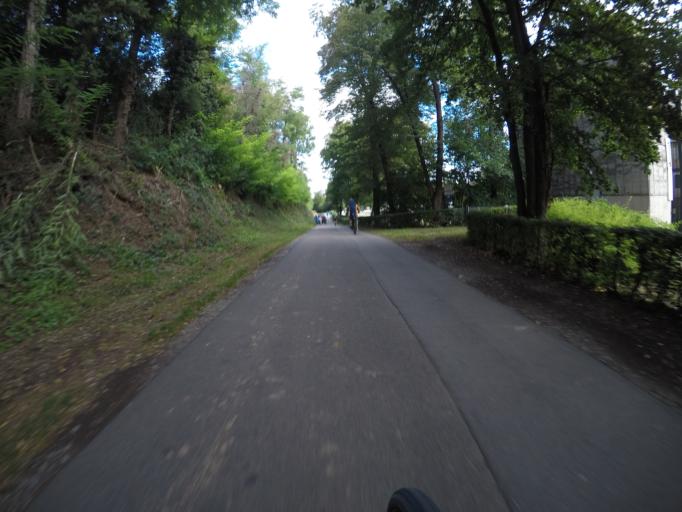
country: DE
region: Baden-Wuerttemberg
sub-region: Regierungsbezirk Stuttgart
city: Marbach am Neckar
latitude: 48.9358
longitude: 9.2489
